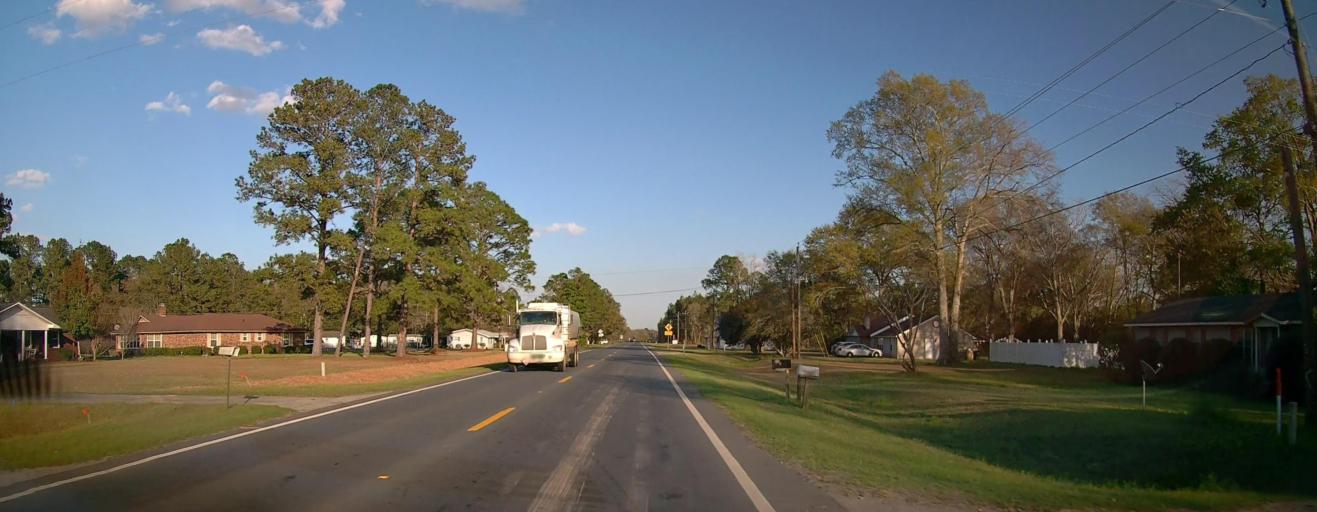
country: US
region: Georgia
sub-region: Evans County
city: Claxton
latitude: 32.1612
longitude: -81.8746
